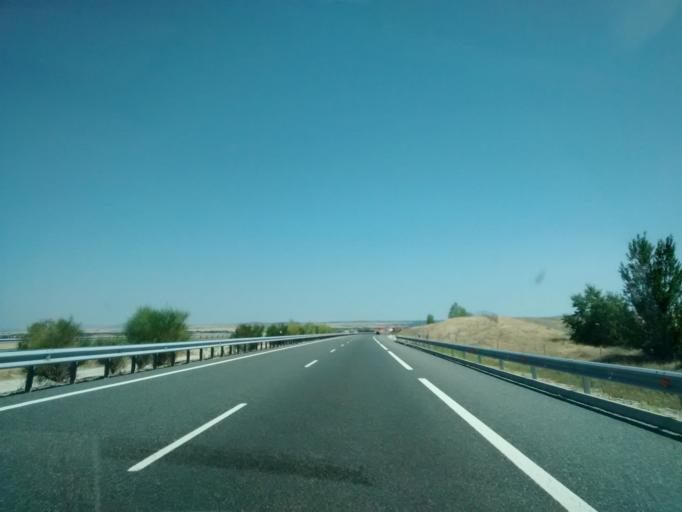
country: ES
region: Castille and Leon
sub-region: Provincia de Avila
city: Munogrande
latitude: 40.8339
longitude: -4.9443
